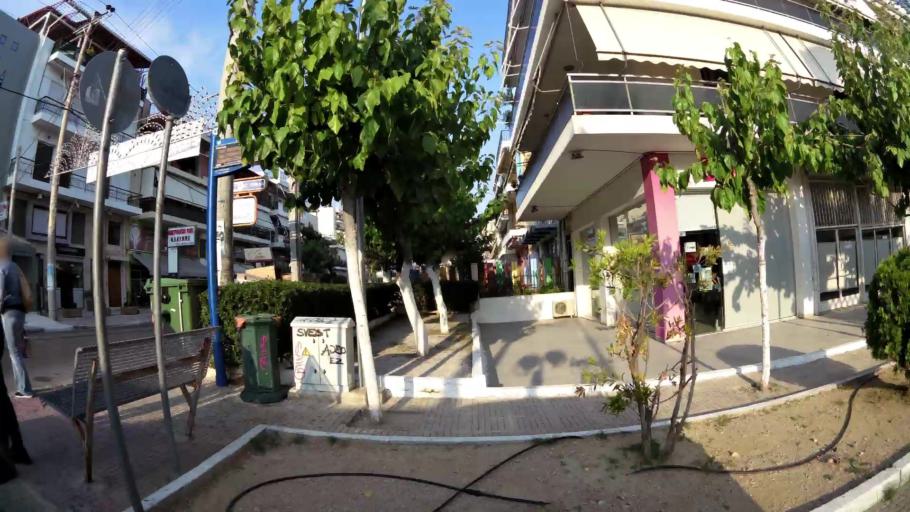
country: GR
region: Attica
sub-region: Nomarchia Athinas
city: Petroupolis
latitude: 38.0397
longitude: 23.6709
